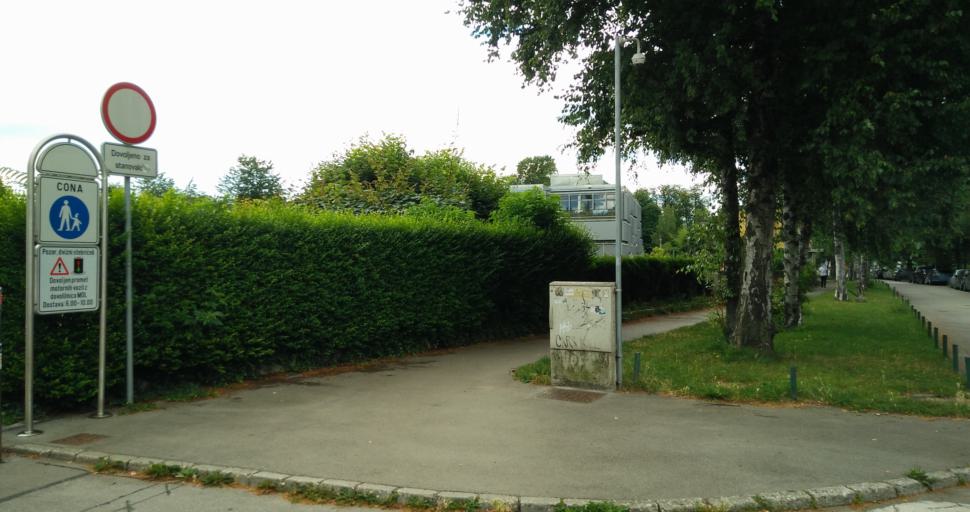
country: SI
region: Ljubljana
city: Ljubljana
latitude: 46.0450
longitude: 14.5024
